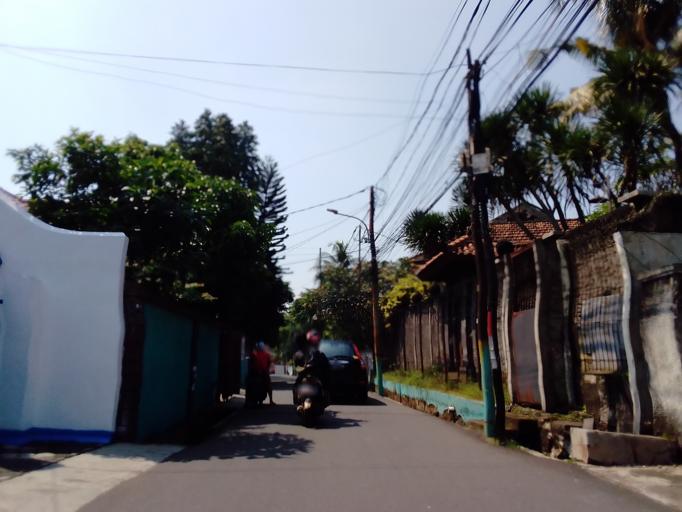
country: ID
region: Jakarta Raya
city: Jakarta
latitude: -6.2622
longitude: 106.8046
